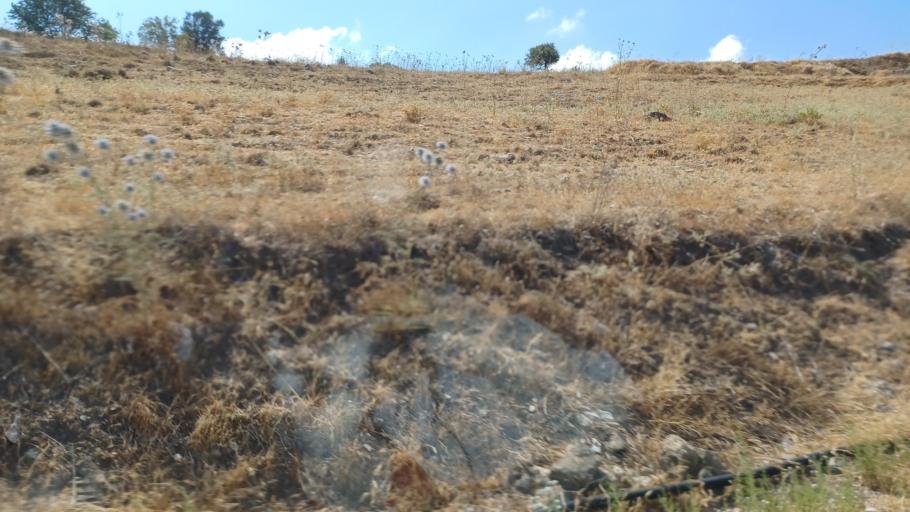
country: CY
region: Pafos
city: Mesogi
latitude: 34.8858
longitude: 32.6109
